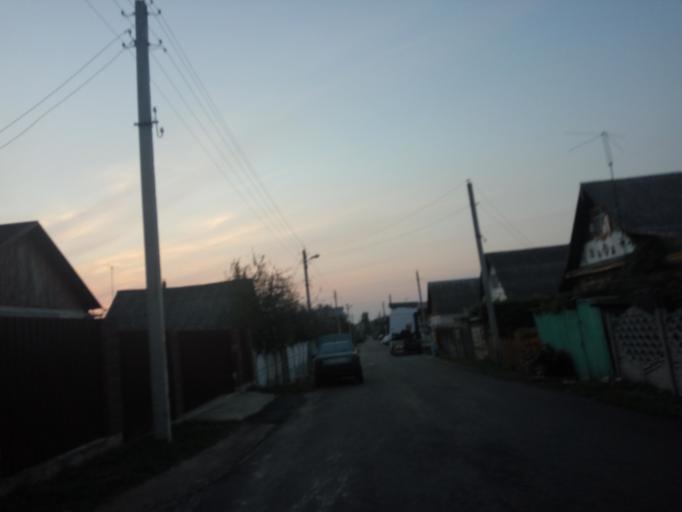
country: BY
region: Vitebsk
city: Vitebsk
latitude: 55.2029
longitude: 30.2470
